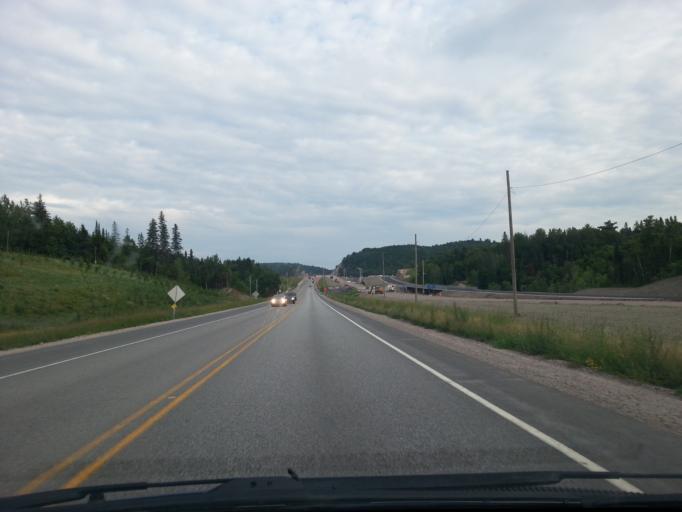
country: CA
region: Quebec
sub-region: Outaouais
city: Wakefield
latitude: 45.6352
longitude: -75.9414
